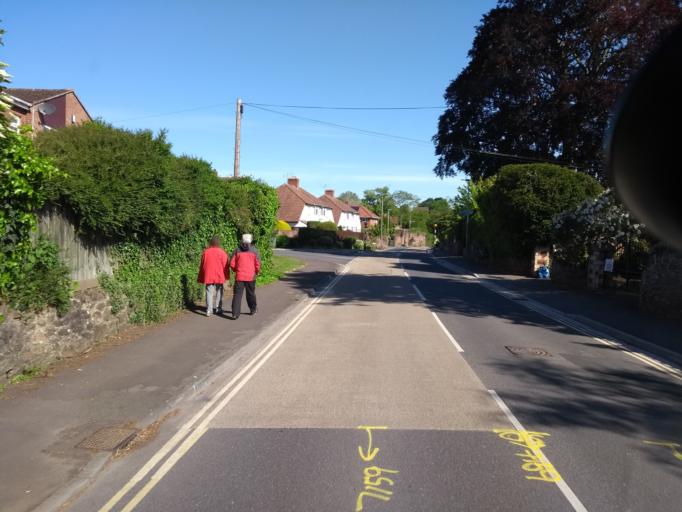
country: GB
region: England
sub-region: Somerset
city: Bridgwater
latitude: 51.1317
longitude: -3.0222
